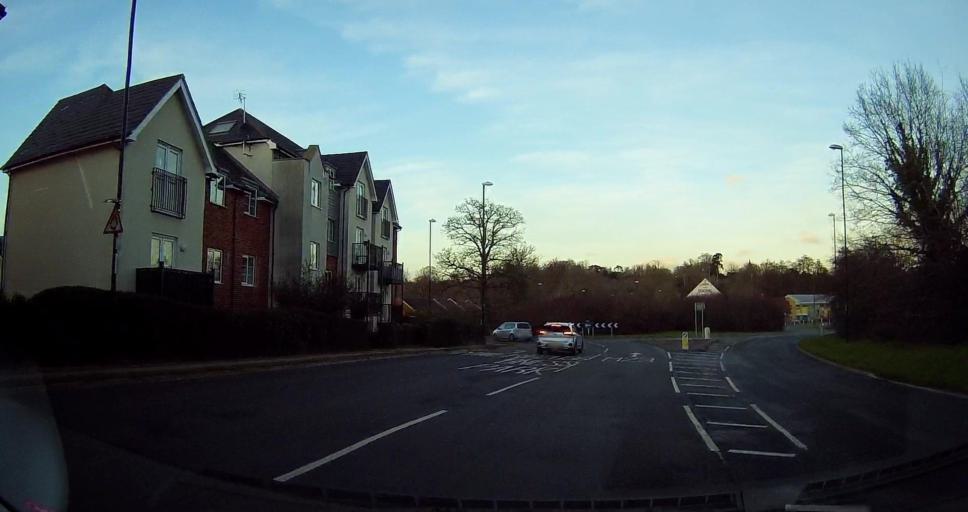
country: GB
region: England
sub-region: West Sussex
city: Maidenbower
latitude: 51.1063
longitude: -0.1455
